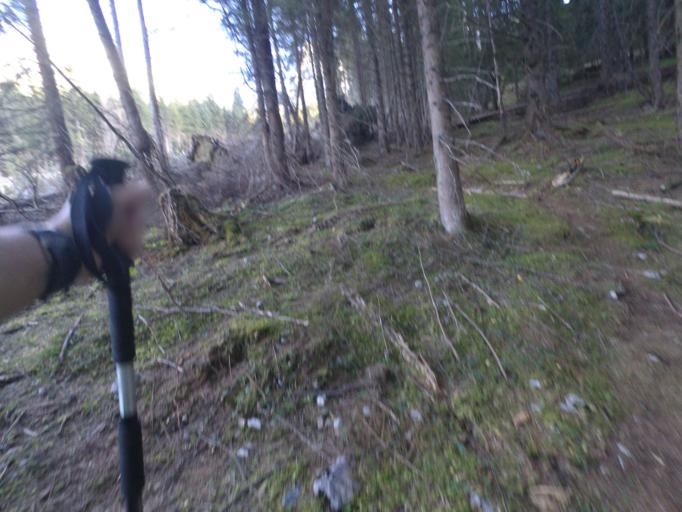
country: AT
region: Salzburg
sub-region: Politischer Bezirk Sankt Johann im Pongau
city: Werfenweng
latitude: 47.4844
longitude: 13.2291
